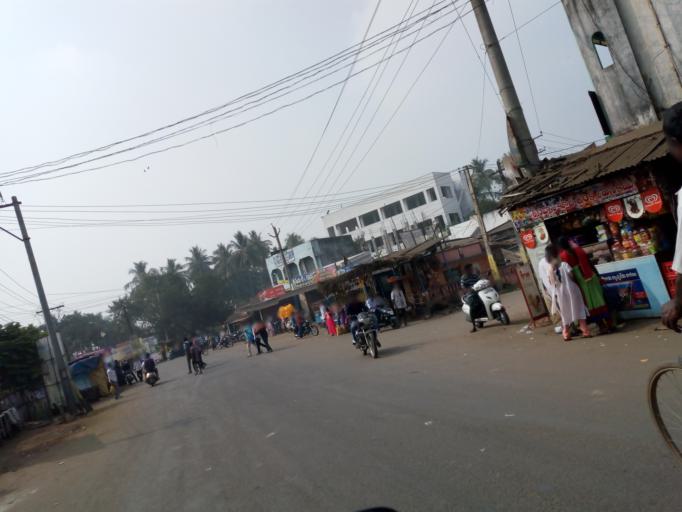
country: IN
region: Andhra Pradesh
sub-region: West Godavari
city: Bhimavaram
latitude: 16.5860
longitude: 81.4673
